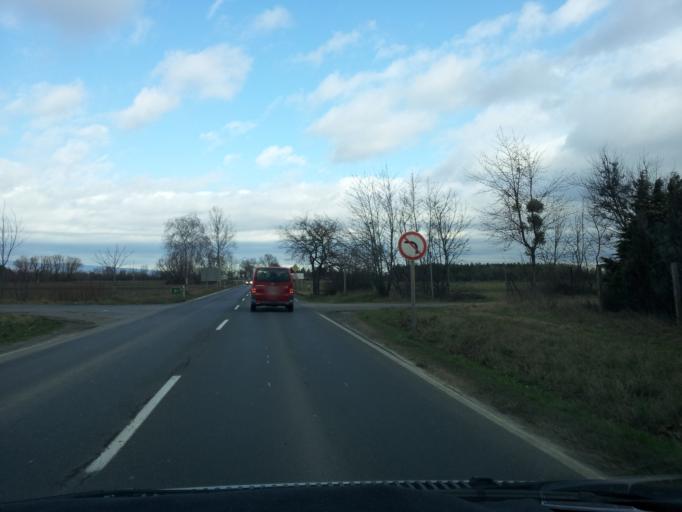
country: HU
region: Vas
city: Gencsapati
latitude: 47.2628
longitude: 16.6111
